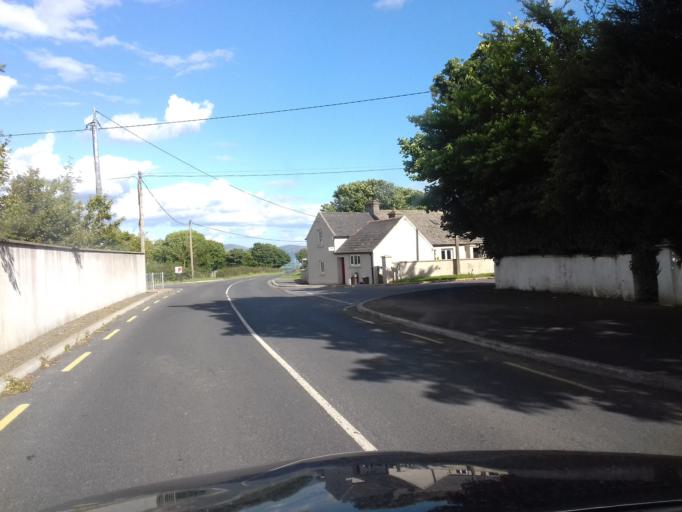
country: IE
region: Leinster
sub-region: Kilkenny
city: Graiguenamanagh
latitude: 52.5471
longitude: -7.0272
